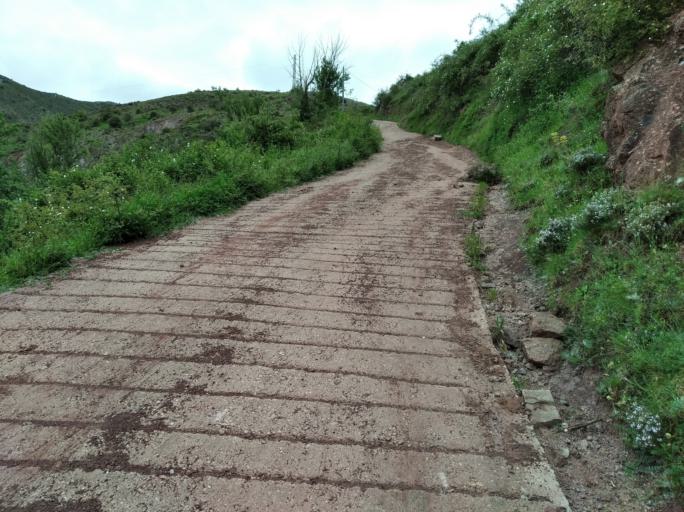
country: ES
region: La Rioja
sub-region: Provincia de La Rioja
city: Robres del Castillo
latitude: 42.2732
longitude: -2.2911
